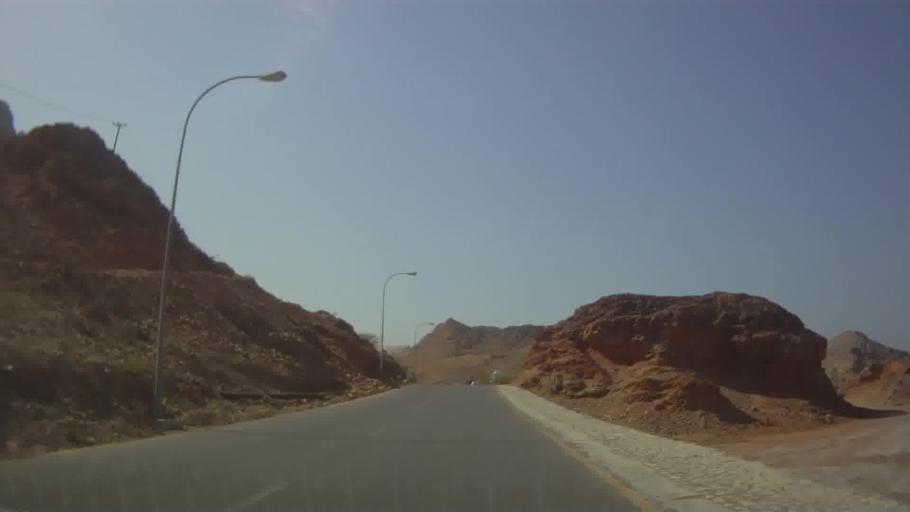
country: OM
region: Muhafazat Masqat
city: Muscat
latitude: 23.5056
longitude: 58.7304
